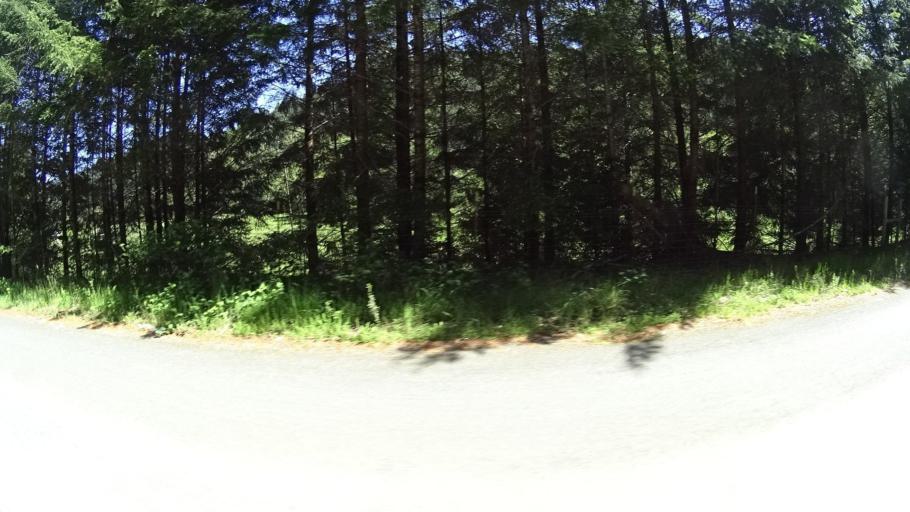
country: US
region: California
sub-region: Humboldt County
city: Rio Dell
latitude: 40.2668
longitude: -124.1988
